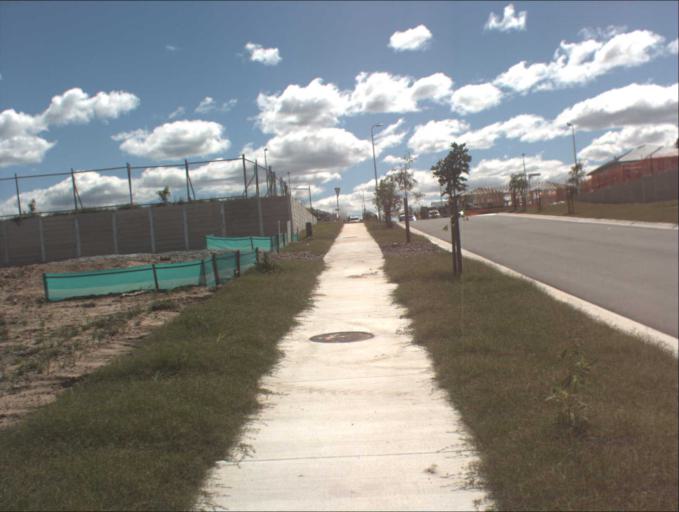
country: AU
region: Queensland
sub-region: Logan
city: Chambers Flat
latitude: -27.8056
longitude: 153.1170
